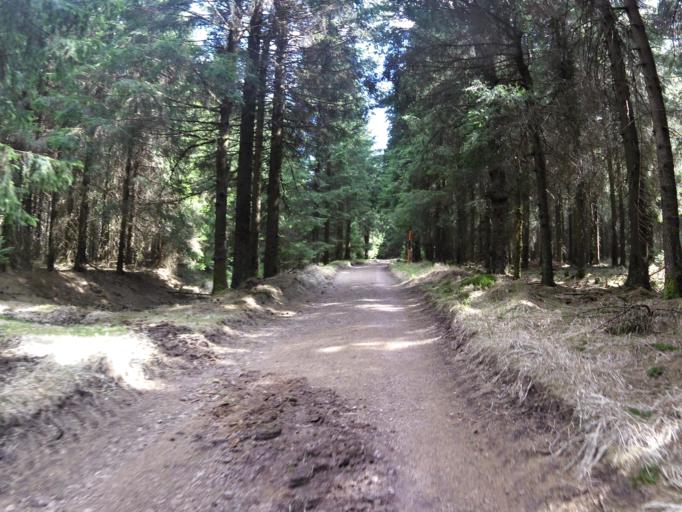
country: DE
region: Thuringia
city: Unterschonau
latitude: 50.7477
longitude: 10.5721
